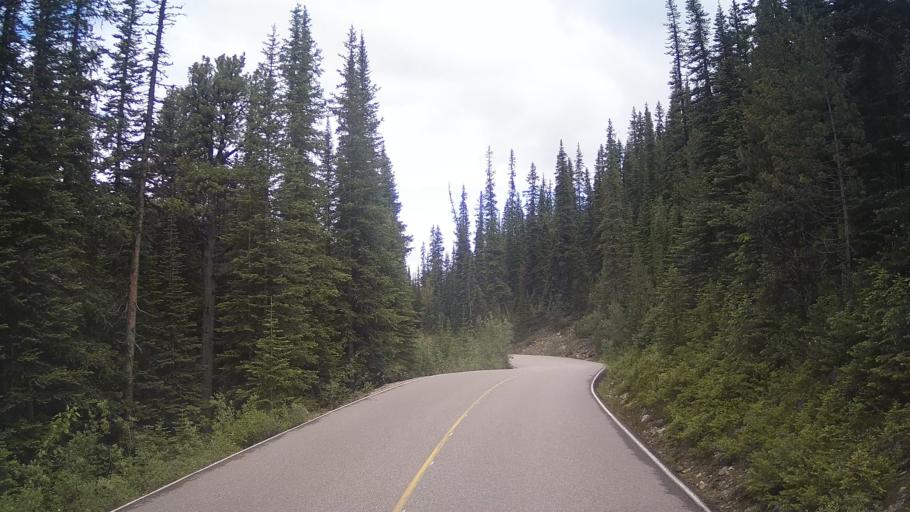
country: CA
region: Alberta
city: Jasper Park Lodge
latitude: 52.6951
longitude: -118.0581
